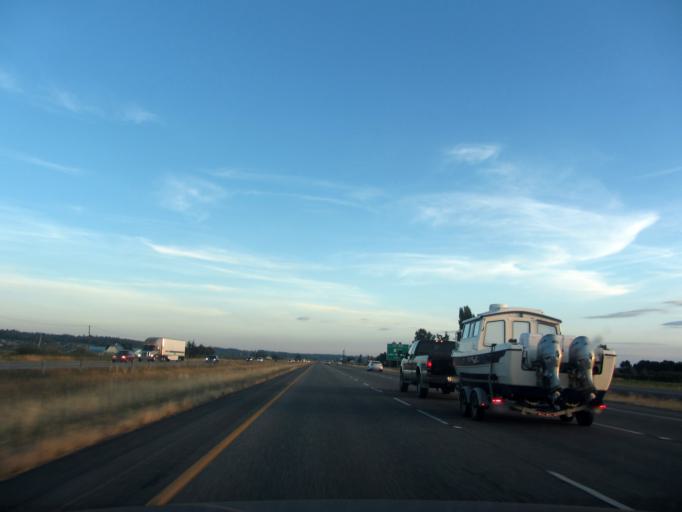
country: US
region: Washington
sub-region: Skagit County
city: Mount Vernon
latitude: 48.3610
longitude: -122.3367
